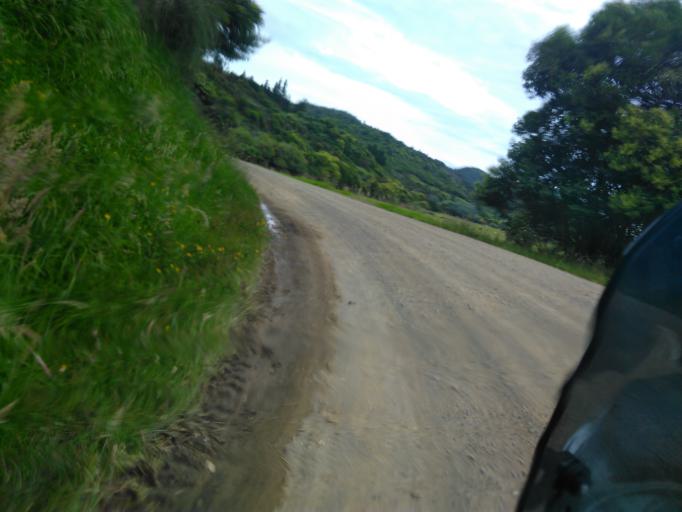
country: NZ
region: Bay of Plenty
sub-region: Opotiki District
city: Opotiki
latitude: -38.0167
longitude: 177.4289
